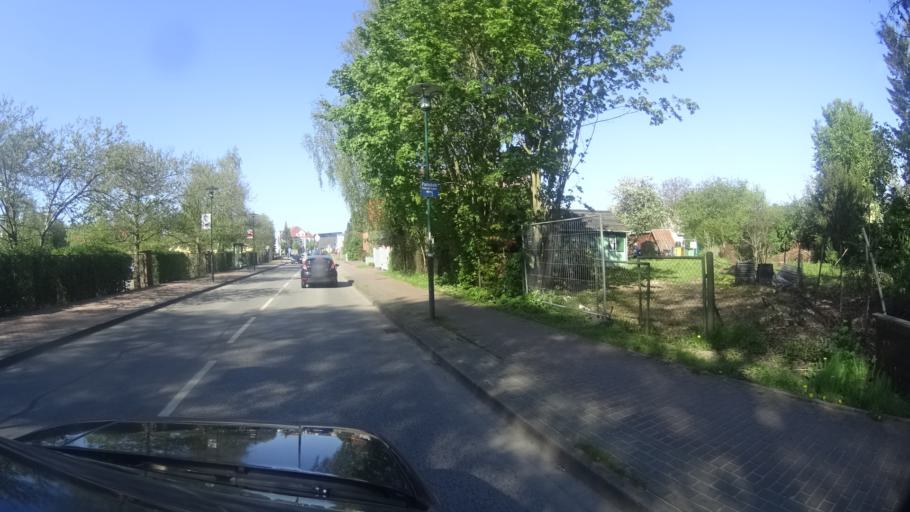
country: DE
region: Mecklenburg-Vorpommern
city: Seeheilbad Graal-Muritz
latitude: 54.2479
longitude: 12.2347
